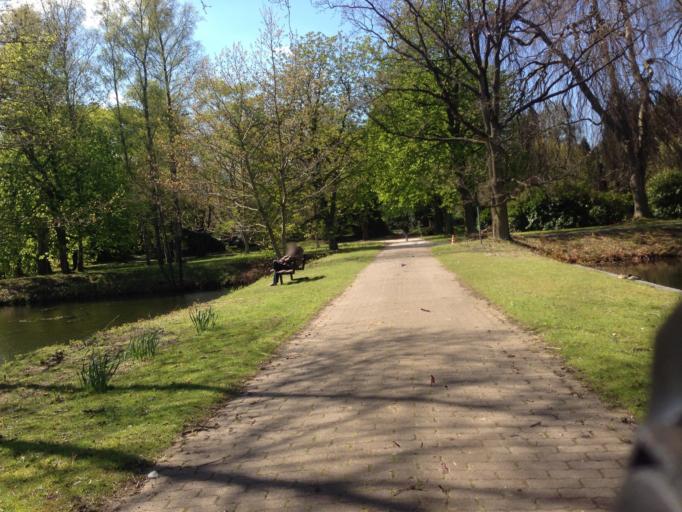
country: DE
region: Hamburg
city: Steilshoop
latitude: 53.6220
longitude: 10.0626
